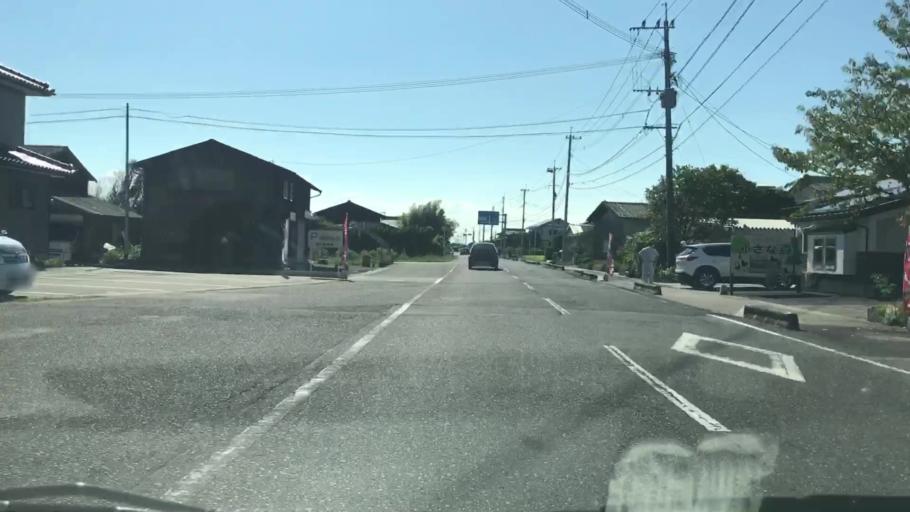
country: JP
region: Saga Prefecture
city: Okawa
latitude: 33.2196
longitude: 130.3376
